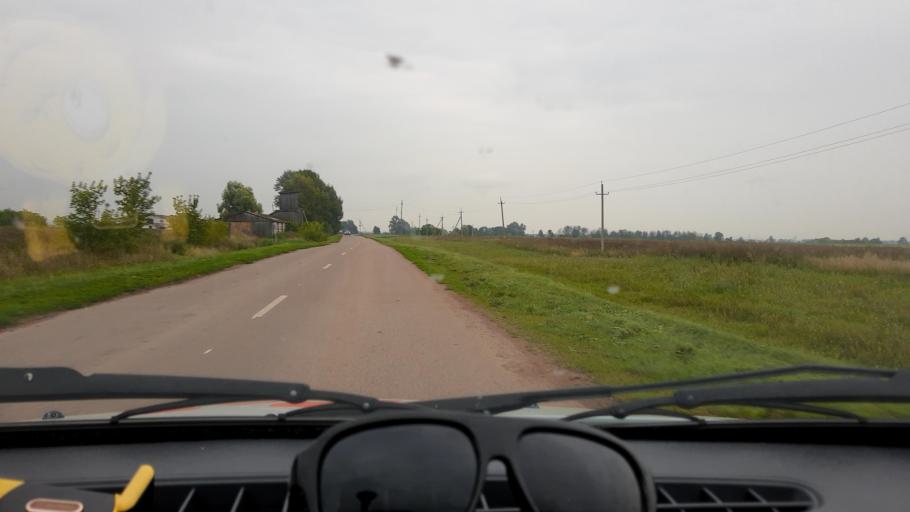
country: RU
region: Bashkortostan
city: Blagoveshchensk
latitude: 55.0092
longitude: 55.7324
